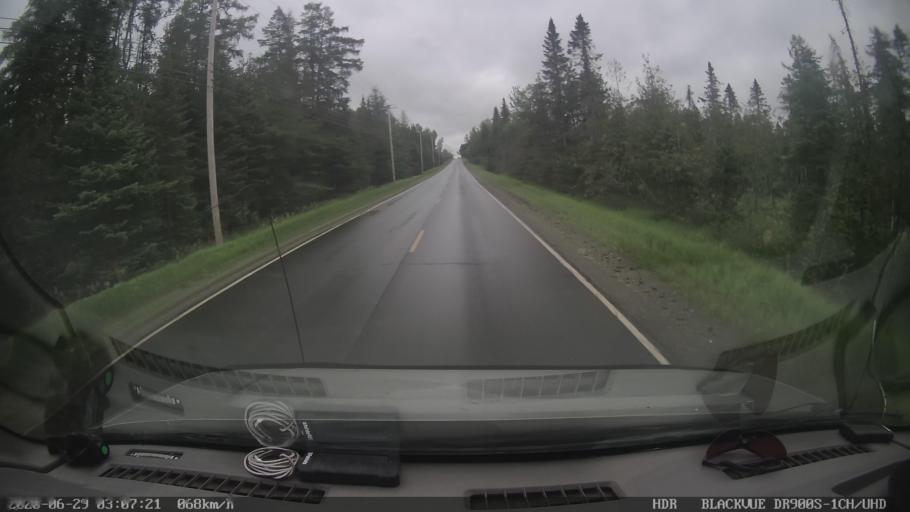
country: US
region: Maine
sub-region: Penobscot County
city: Patten
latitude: 45.8758
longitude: -68.4713
